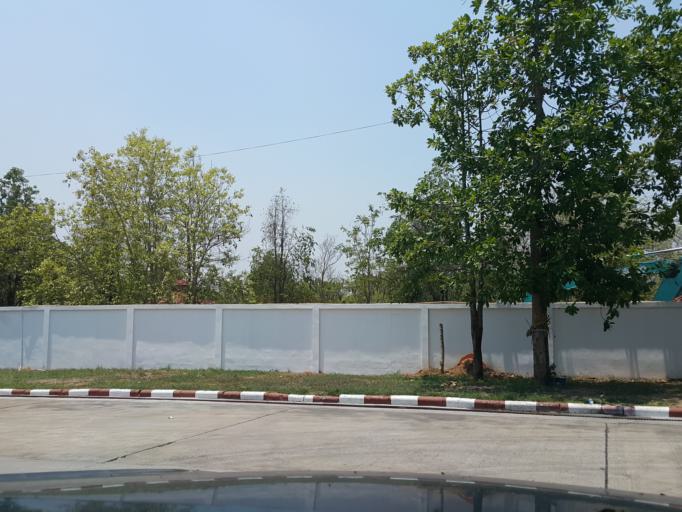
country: TH
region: Lampang
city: Thoen
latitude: 17.5434
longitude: 99.1956
